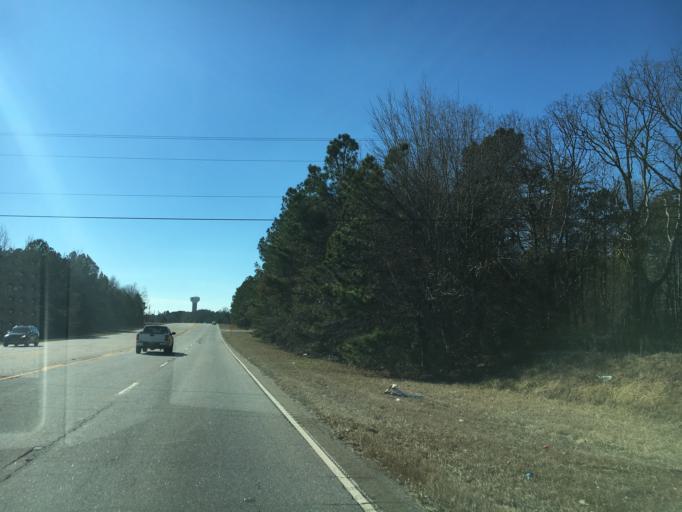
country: US
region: South Carolina
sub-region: Anderson County
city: Homeland Park
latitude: 34.4199
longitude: -82.6732
